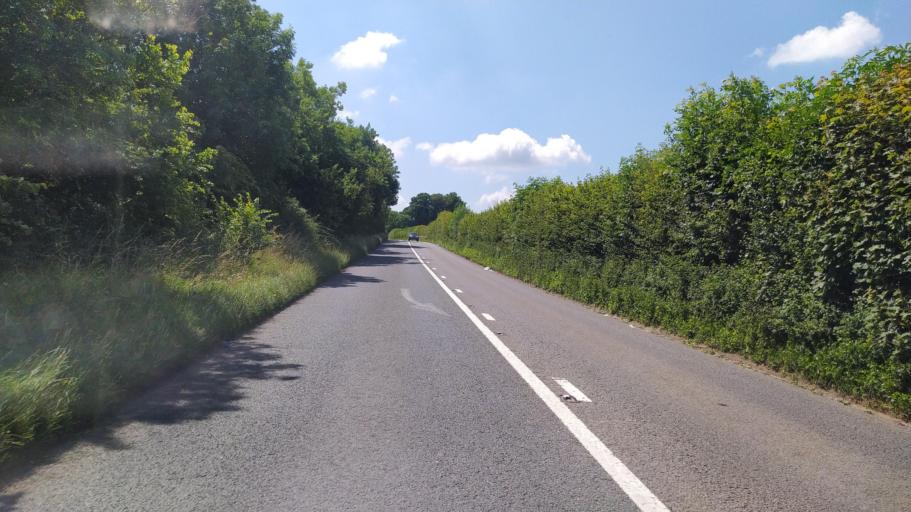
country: GB
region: England
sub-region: Somerset
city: Frome
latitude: 51.2144
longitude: -2.3379
